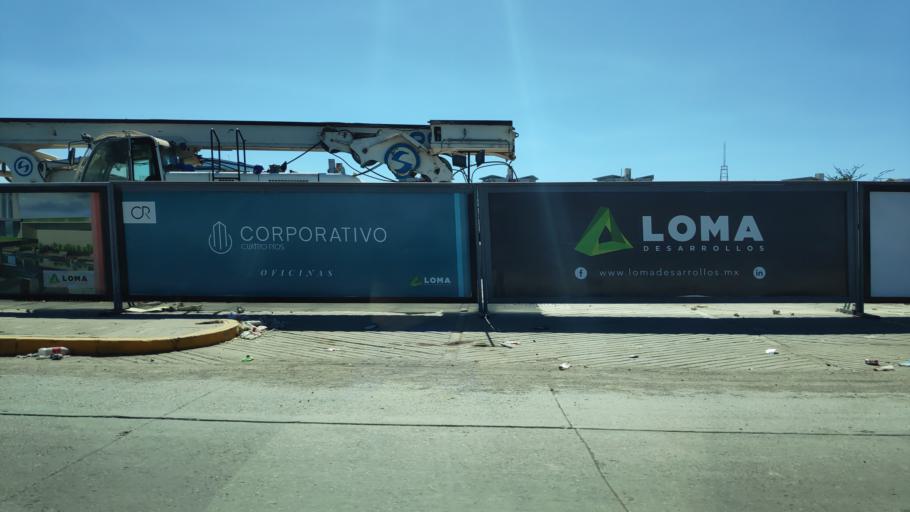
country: MX
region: Sinaloa
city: Culiacan
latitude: 24.8245
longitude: -107.4001
